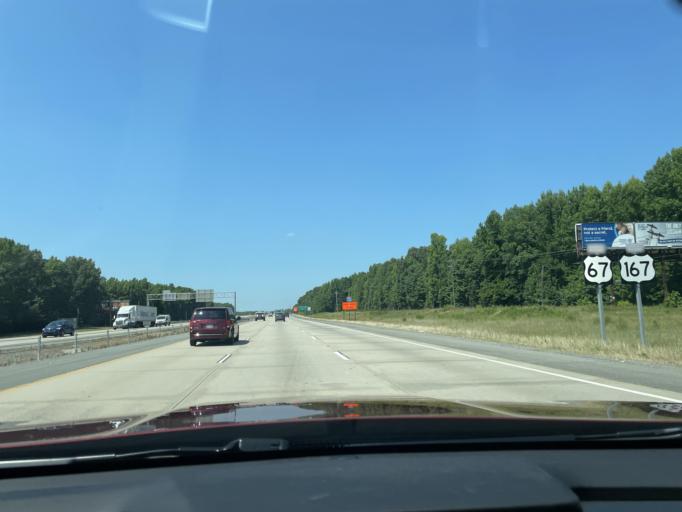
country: US
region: Arkansas
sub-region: Pulaski County
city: Jacksonville
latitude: 34.8542
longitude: -92.1381
